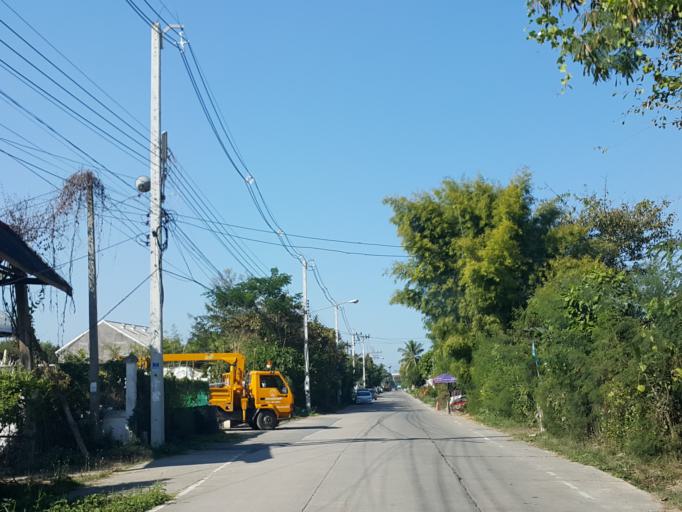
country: TH
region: Chiang Mai
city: San Sai
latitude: 18.8790
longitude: 99.0133
